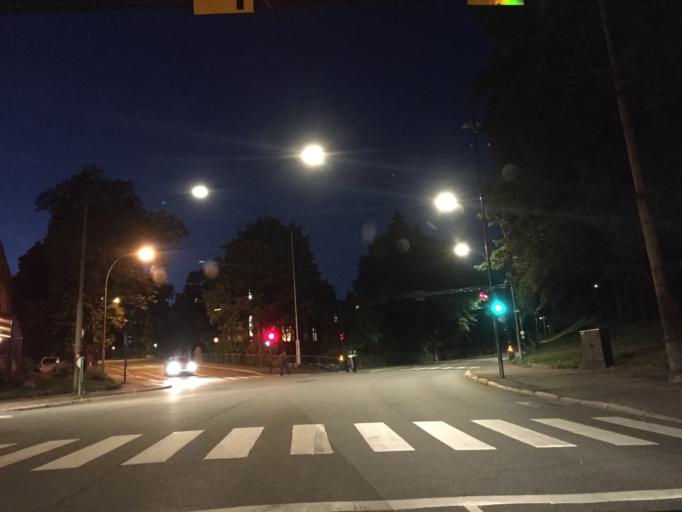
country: NO
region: Oslo
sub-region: Oslo
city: Oslo
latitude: 59.9273
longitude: 10.7388
